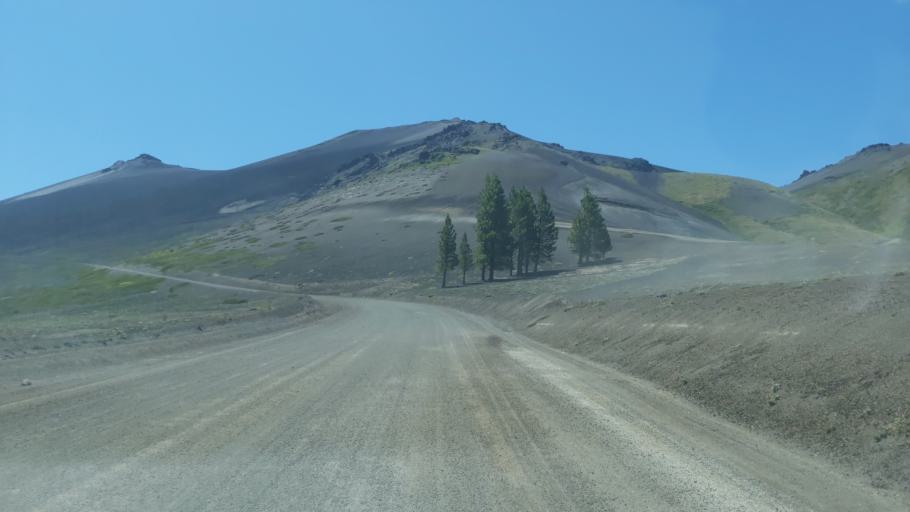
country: CL
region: Araucania
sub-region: Provincia de Cautin
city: Vilcun
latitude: -38.4156
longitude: -71.5425
